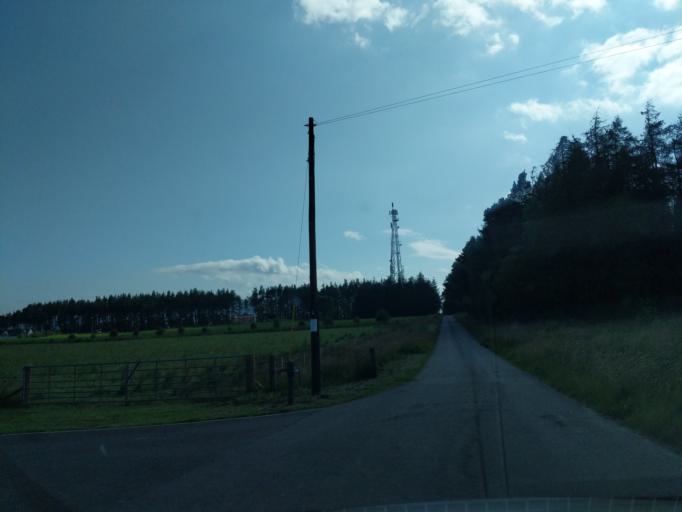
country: GB
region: Scotland
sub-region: Moray
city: Rothes
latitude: 57.4852
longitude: -3.2298
